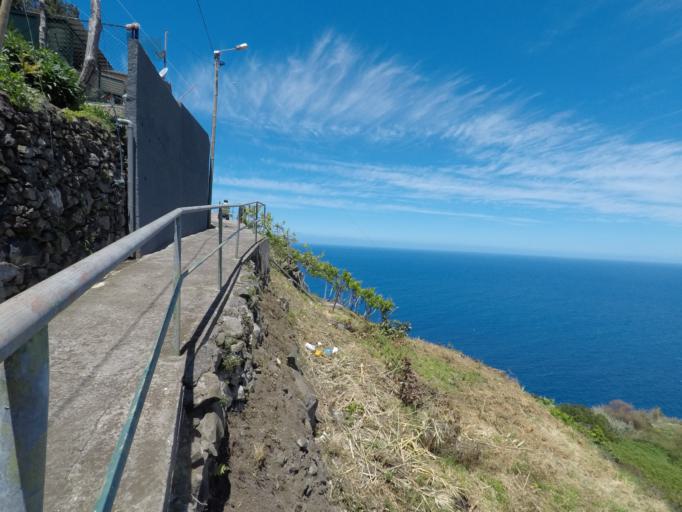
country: PT
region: Madeira
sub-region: Sao Vicente
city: Sao Vicente
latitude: 32.8258
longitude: -16.9792
